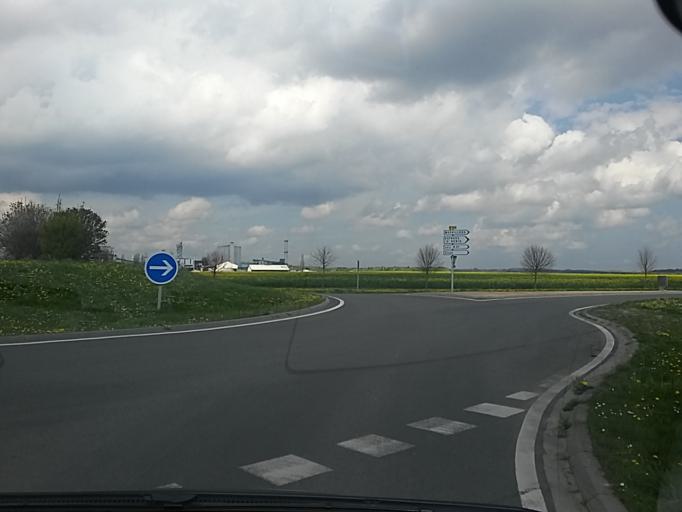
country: FR
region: Picardie
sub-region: Departement de l'Oise
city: Chevrieres
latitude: 49.3532
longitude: 2.6737
